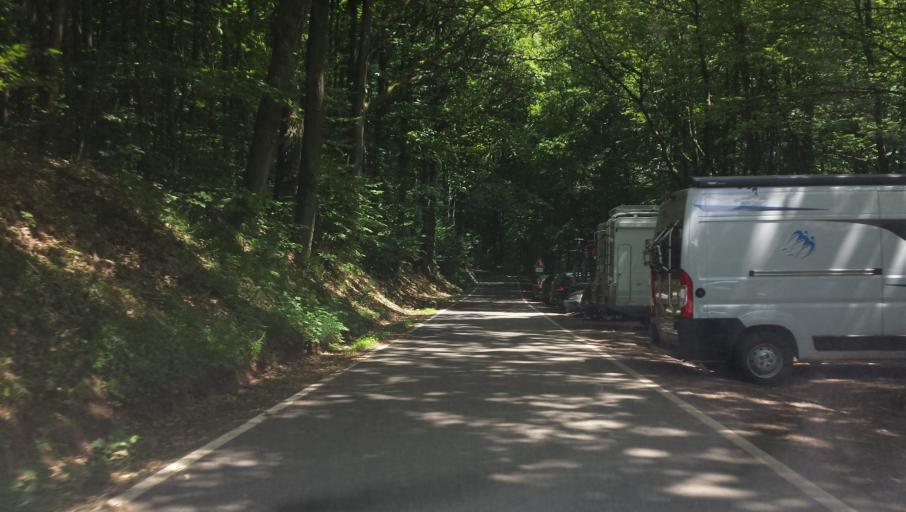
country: DE
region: Rheinland-Pfalz
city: Waldhambach
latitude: 49.1868
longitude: 7.9845
